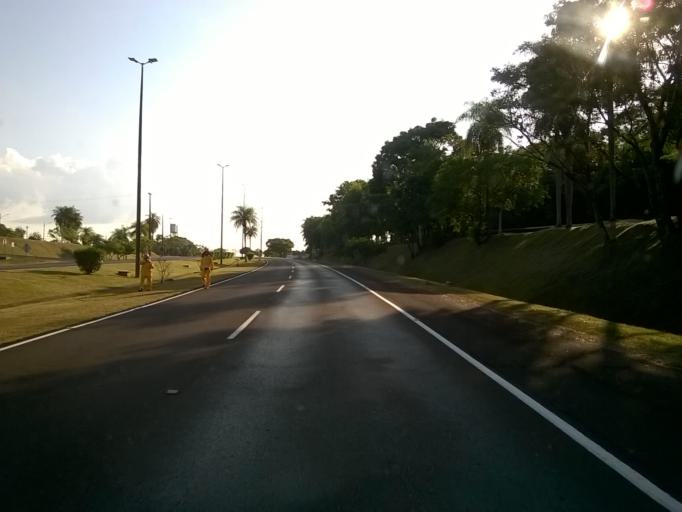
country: PY
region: Alto Parana
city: Ciudad del Este
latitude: -25.4202
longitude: -54.6204
